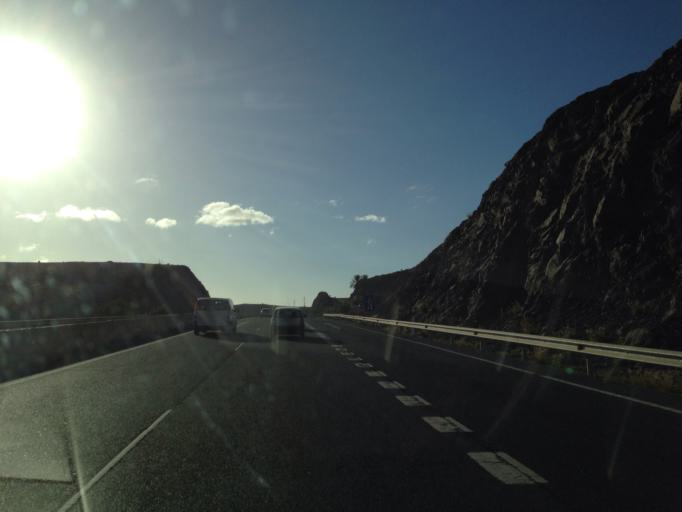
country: ES
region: Canary Islands
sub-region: Provincia de Las Palmas
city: Maspalomas
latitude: 27.7710
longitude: -15.6396
